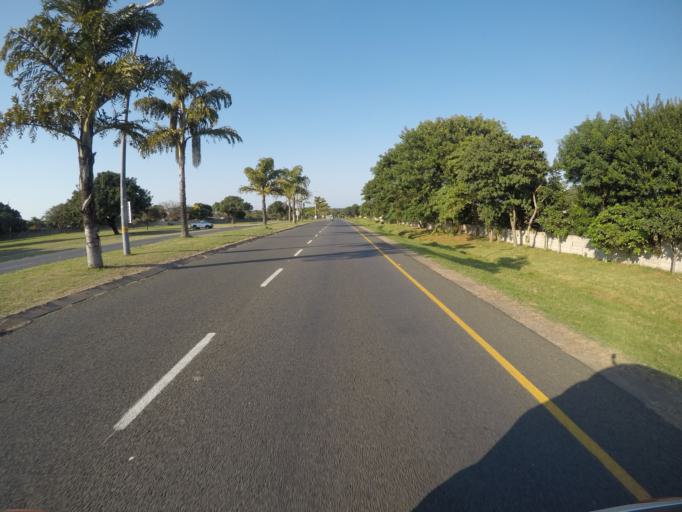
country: ZA
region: KwaZulu-Natal
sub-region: uThungulu District Municipality
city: Richards Bay
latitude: -28.7635
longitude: 32.0593
